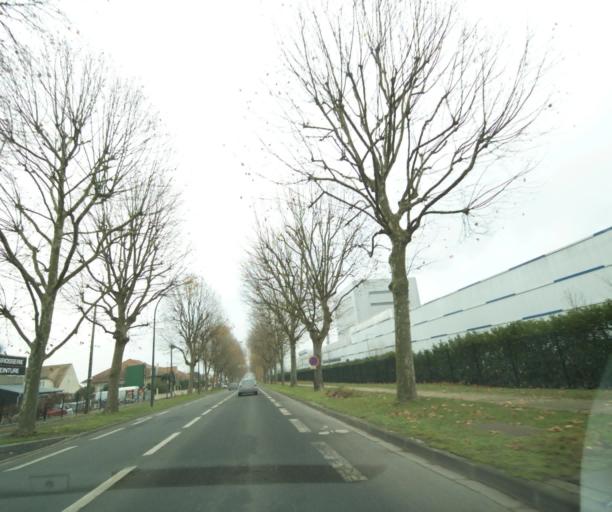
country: FR
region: Ile-de-France
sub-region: Departement de Seine-Saint-Denis
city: Vaujours
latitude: 48.9374
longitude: 2.5916
